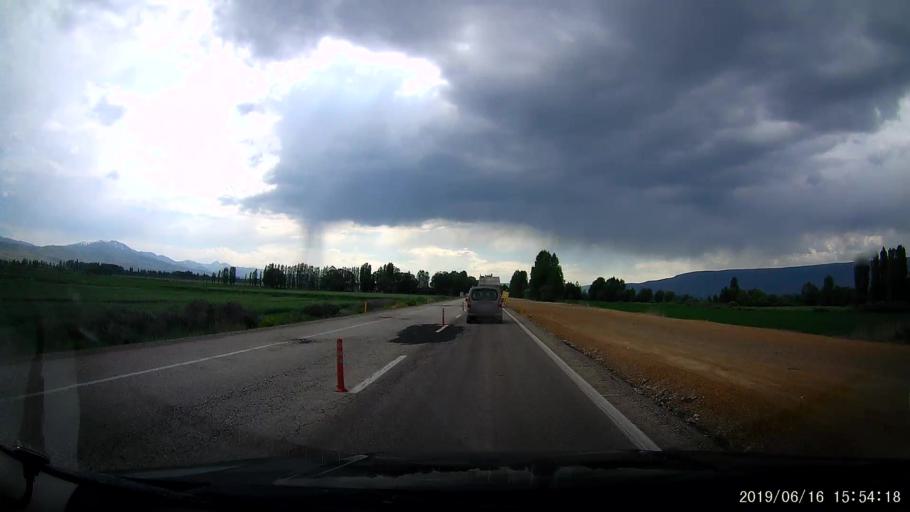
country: TR
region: Erzurum
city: Pasinler
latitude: 39.9776
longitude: 41.6357
